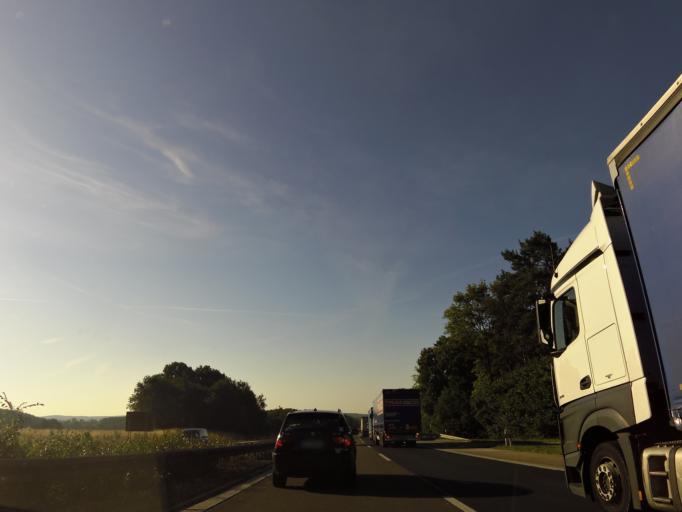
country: DE
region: Bavaria
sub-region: Regierungsbezirk Mittelfranken
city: Gremsdorf
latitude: 49.7119
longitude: 10.8447
